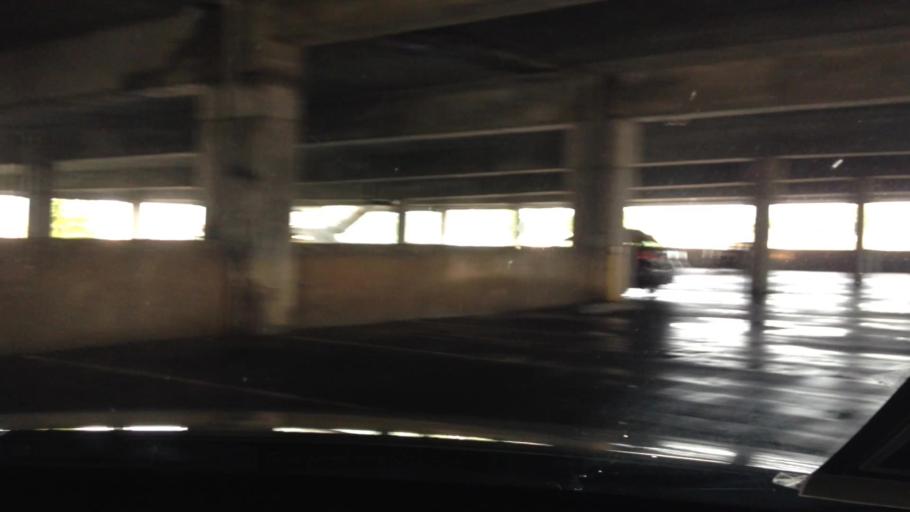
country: US
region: Kansas
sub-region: Wyandotte County
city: Edwardsville
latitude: 39.1278
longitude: -94.8271
